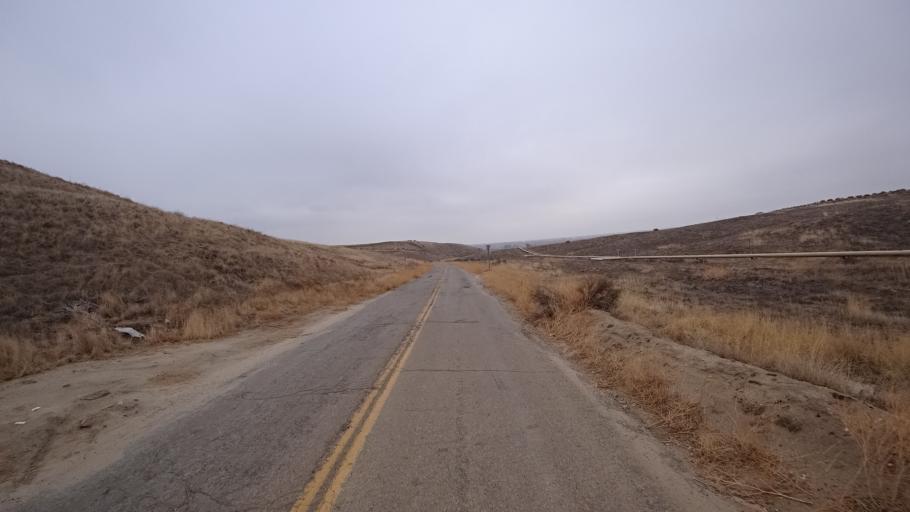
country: US
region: California
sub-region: Kern County
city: Oildale
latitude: 35.4230
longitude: -118.9359
